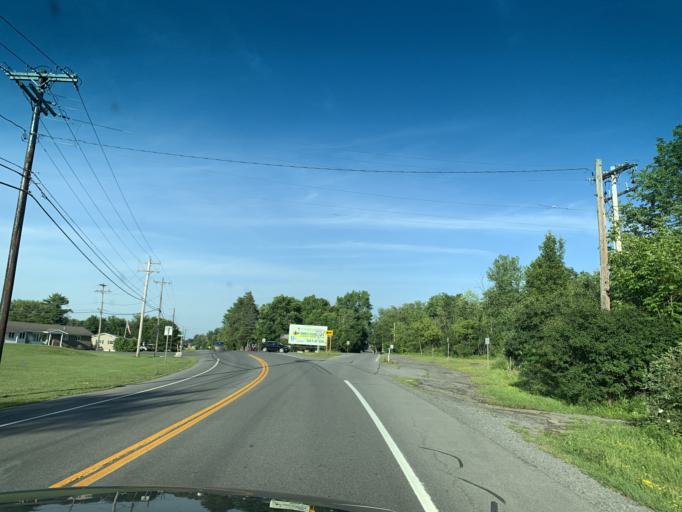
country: US
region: New York
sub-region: Oneida County
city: New Hartford
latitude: 43.0711
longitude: -75.3288
